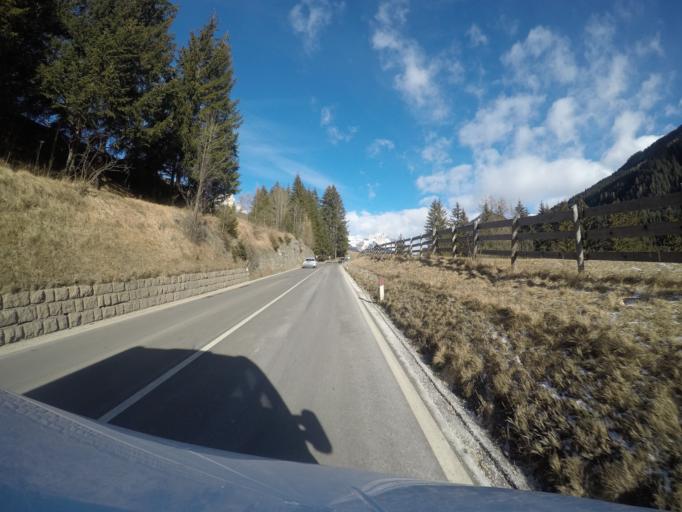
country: IT
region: Trentino-Alto Adige
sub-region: Provincia di Trento
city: Vigo di Fassa
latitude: 46.4139
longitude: 11.6781
